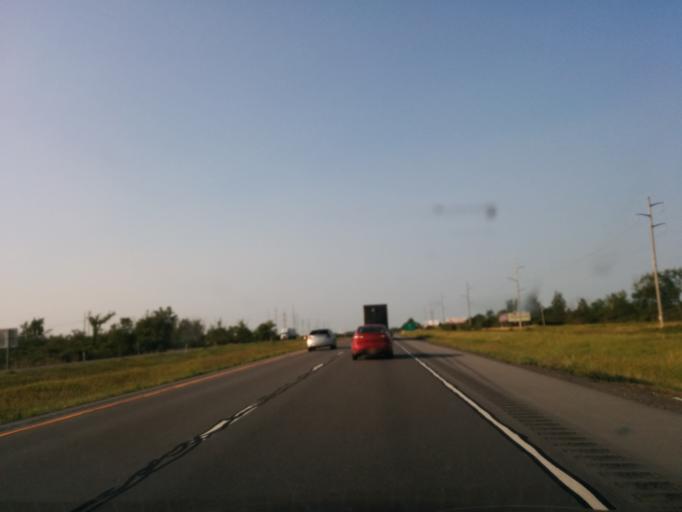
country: US
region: New York
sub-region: Jefferson County
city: Watertown
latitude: 43.9545
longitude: -75.9540
